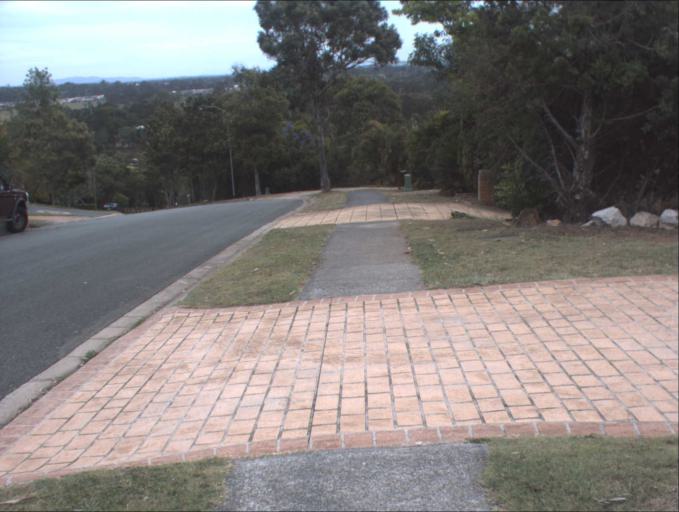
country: AU
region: Queensland
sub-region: Logan
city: Slacks Creek
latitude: -27.6752
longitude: 153.1698
